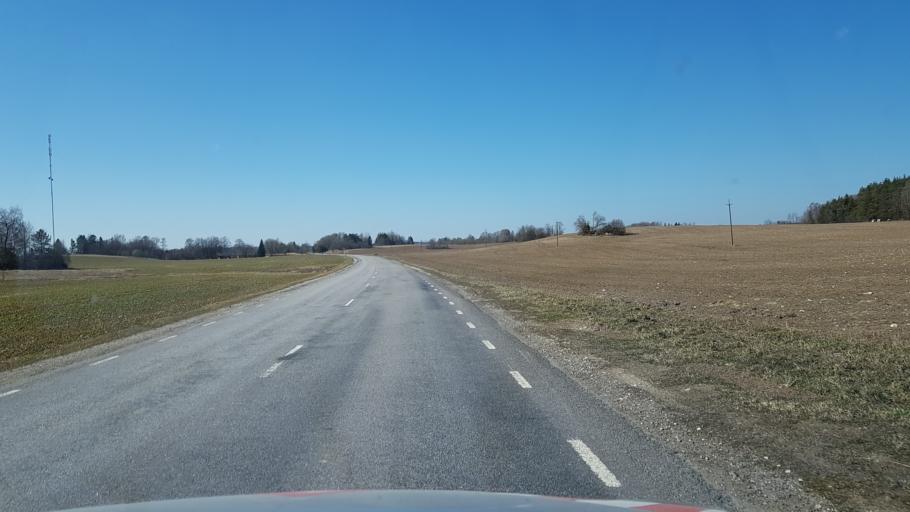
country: EE
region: Laeaene-Virumaa
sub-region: Tamsalu vald
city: Tamsalu
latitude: 59.1660
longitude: 26.1753
